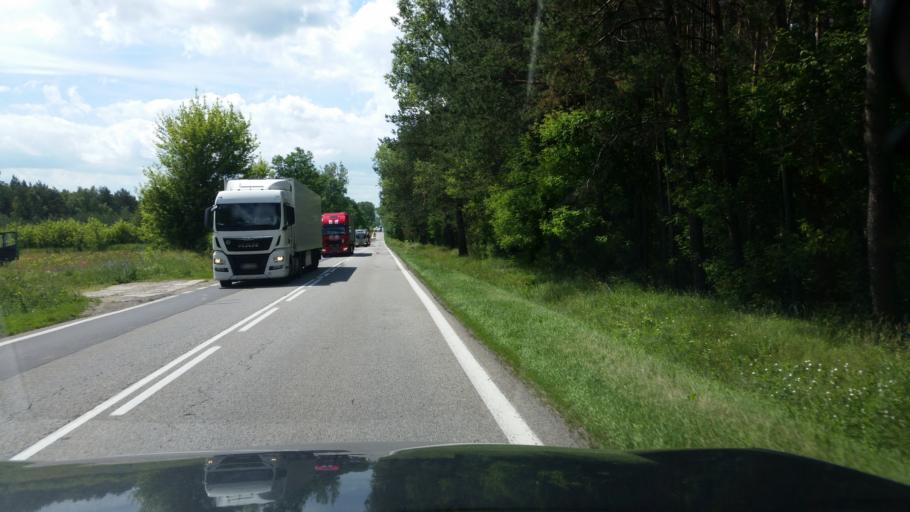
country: PL
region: Podlasie
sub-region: Powiat kolnenski
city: Stawiski
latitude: 53.2872
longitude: 22.1417
